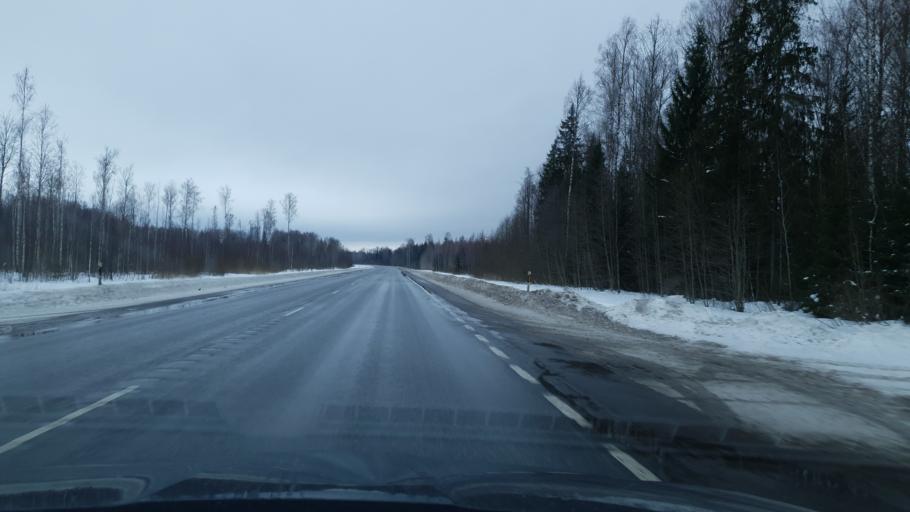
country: EE
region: Tartu
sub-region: Puhja vald
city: Puhja
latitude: 58.5000
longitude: 26.3304
